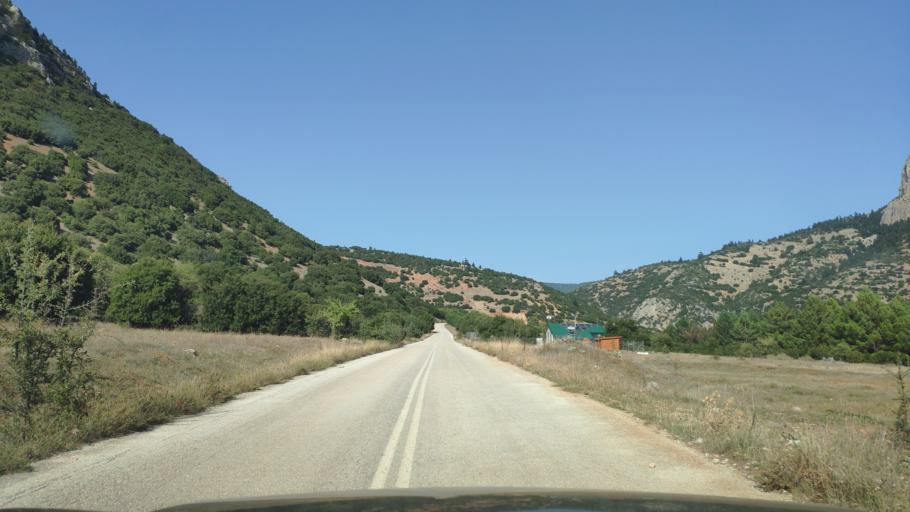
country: GR
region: West Greece
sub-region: Nomos Achaias
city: Aiyira
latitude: 37.9645
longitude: 22.3465
